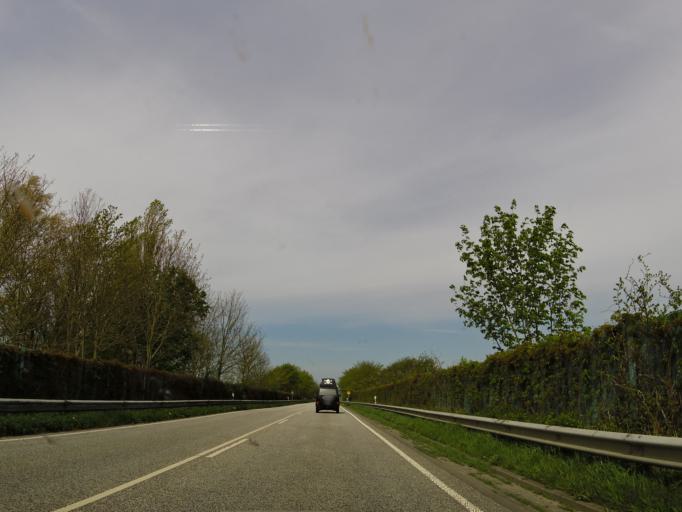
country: DE
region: Schleswig-Holstein
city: Groven
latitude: 54.2919
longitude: 8.9800
